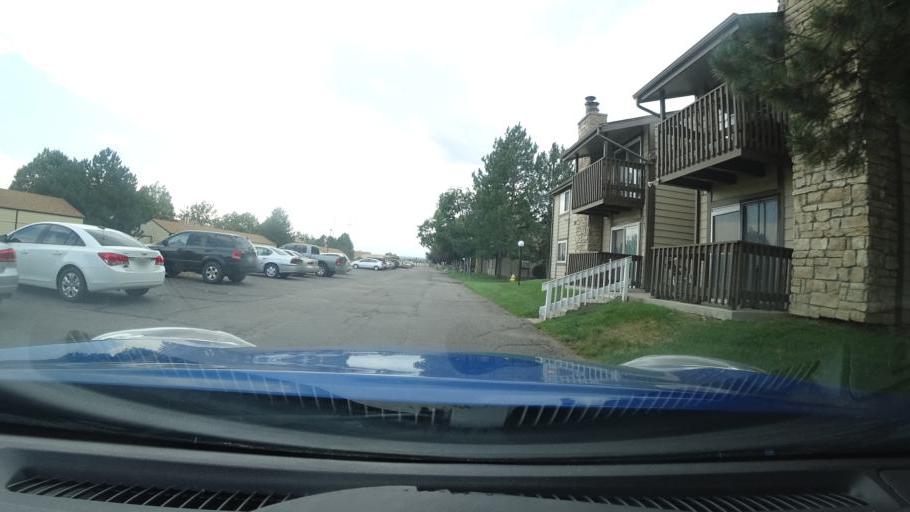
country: US
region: Colorado
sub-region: Adams County
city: Aurora
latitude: 39.6840
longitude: -104.7870
